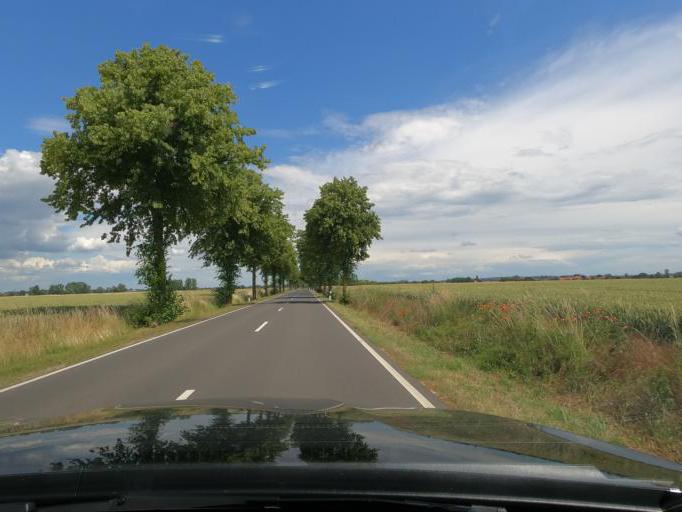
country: DE
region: Lower Saxony
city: Schellerten
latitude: 52.1683
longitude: 10.0752
